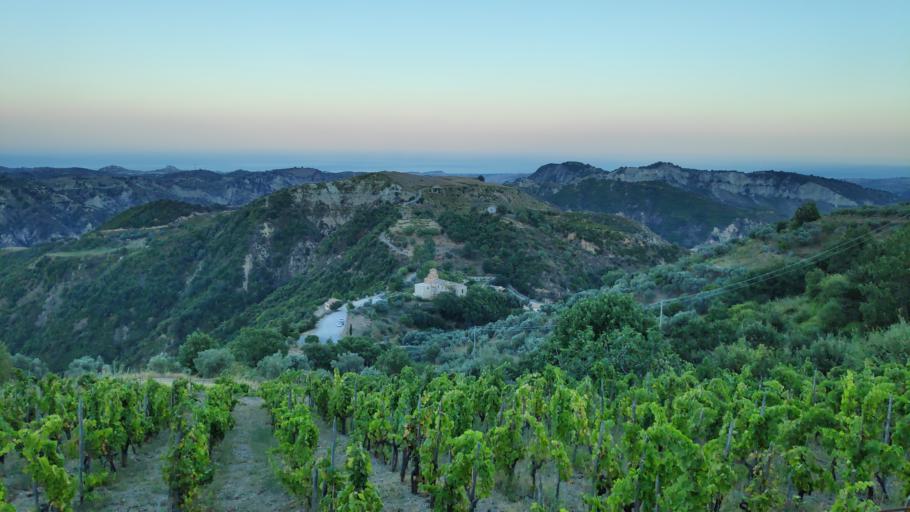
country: IT
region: Calabria
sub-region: Provincia di Reggio Calabria
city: Bivongi
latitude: 38.4958
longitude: 16.4672
